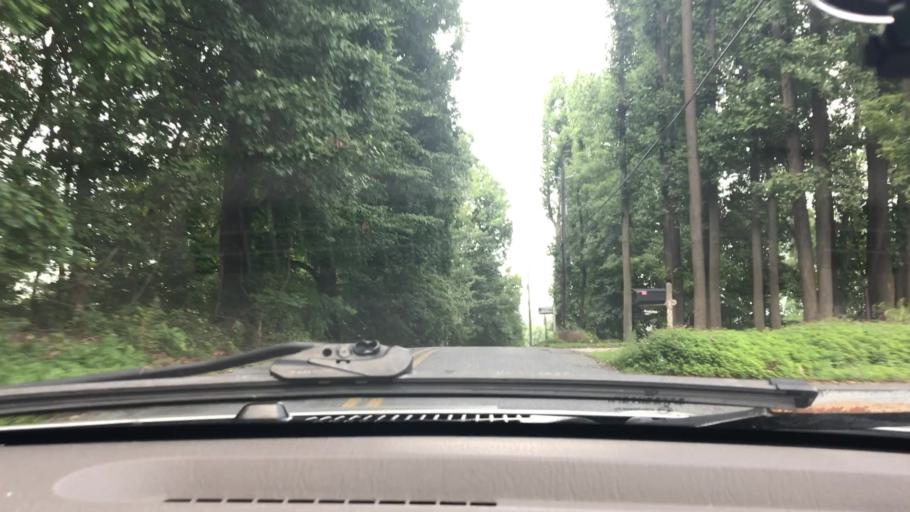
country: US
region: Pennsylvania
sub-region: Lancaster County
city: Elizabethtown
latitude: 40.1660
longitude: -76.6186
